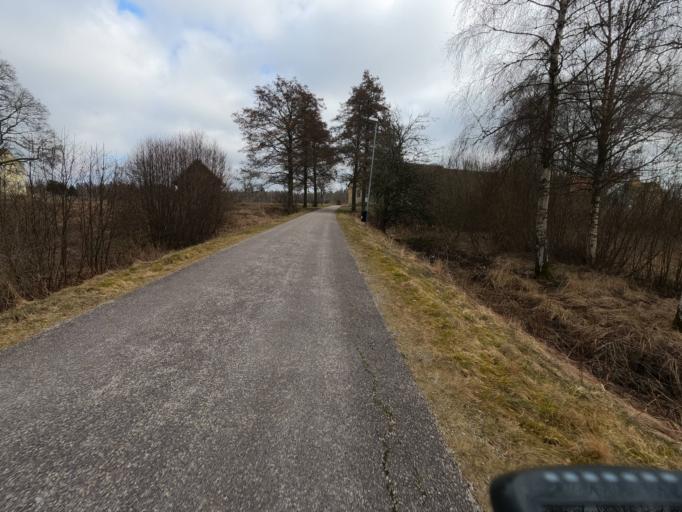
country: SE
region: Joenkoeping
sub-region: Varnamo Kommun
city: Rydaholm
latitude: 56.8619
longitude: 14.1713
